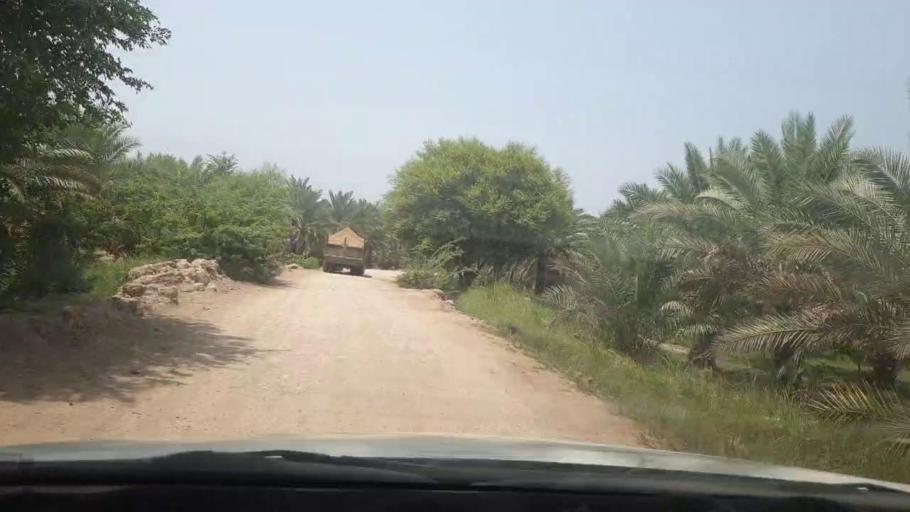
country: PK
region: Sindh
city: Khairpur
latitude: 27.5004
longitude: 68.8745
